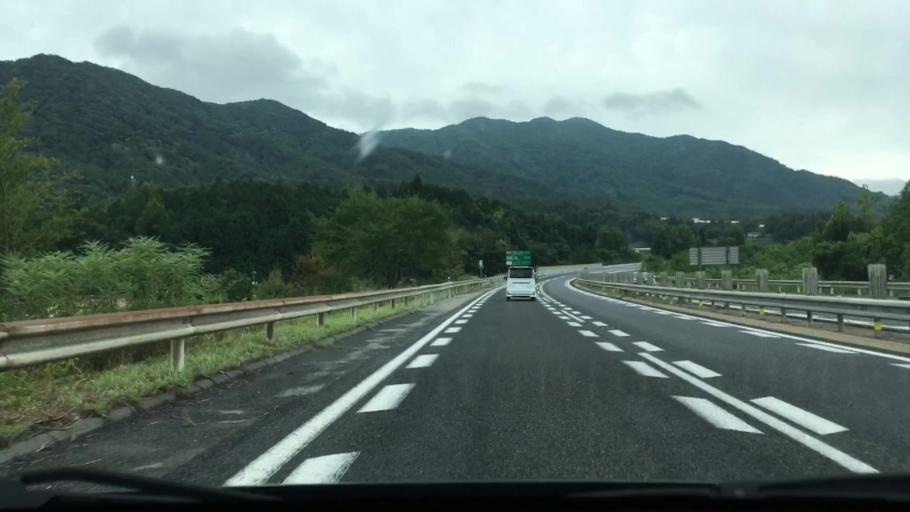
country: JP
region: Hiroshima
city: Hiroshima-shi
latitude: 34.6461
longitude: 132.5171
